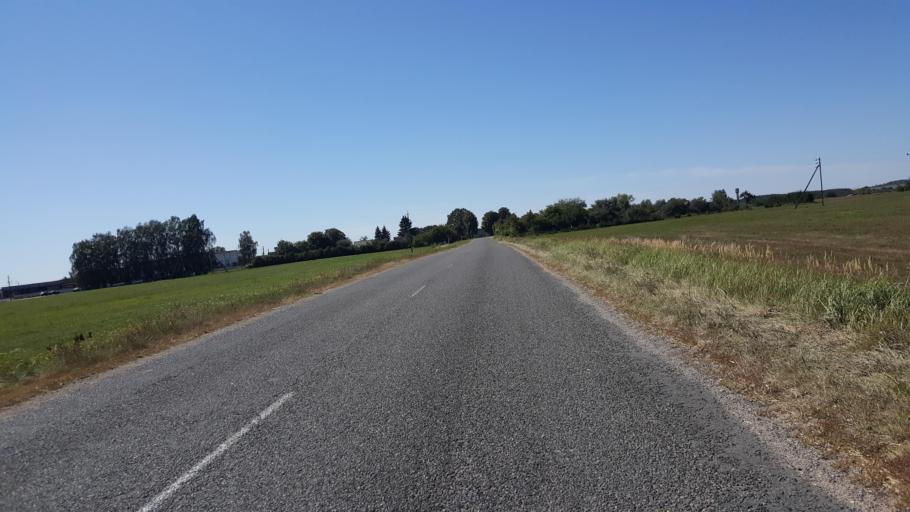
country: PL
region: Lublin Voivodeship
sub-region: Powiat bialski
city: Rokitno
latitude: 52.2296
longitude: 23.3577
